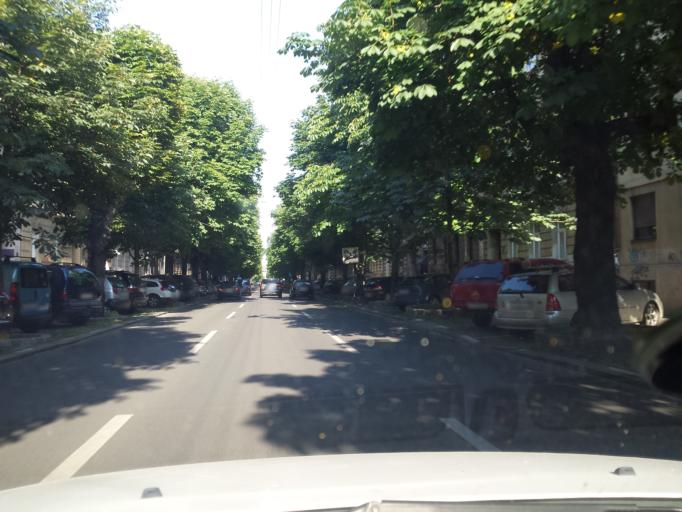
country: HR
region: Grad Zagreb
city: Zagreb - Centar
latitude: 45.8107
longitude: 15.9612
